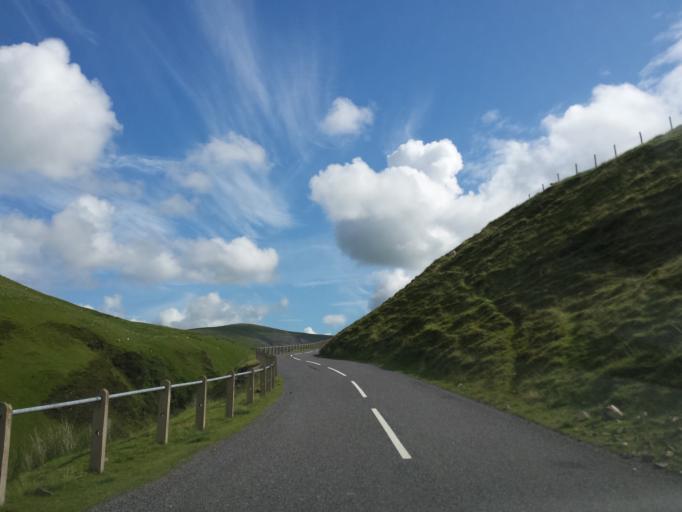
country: GB
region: Scotland
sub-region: Dumfries and Galloway
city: Moffat
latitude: 55.4263
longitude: -3.2704
